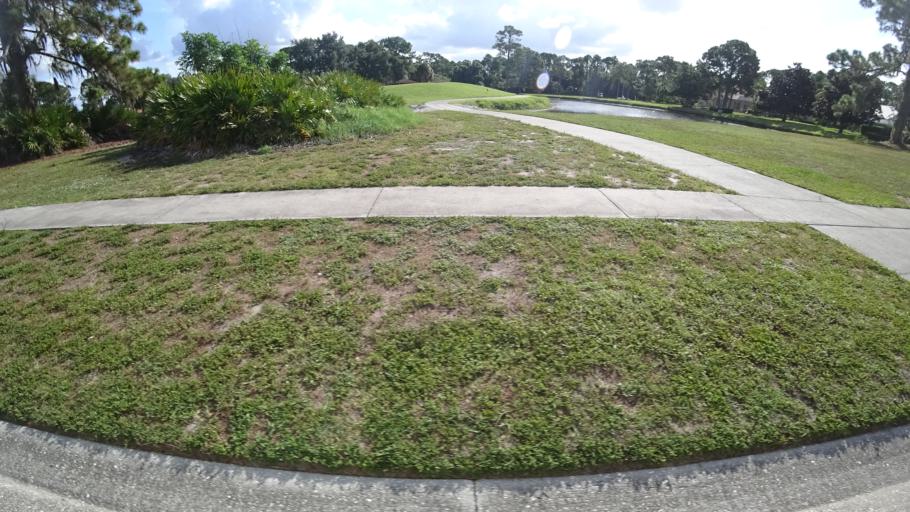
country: US
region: Florida
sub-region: Sarasota County
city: Desoto Lakes
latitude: 27.4025
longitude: -82.4845
